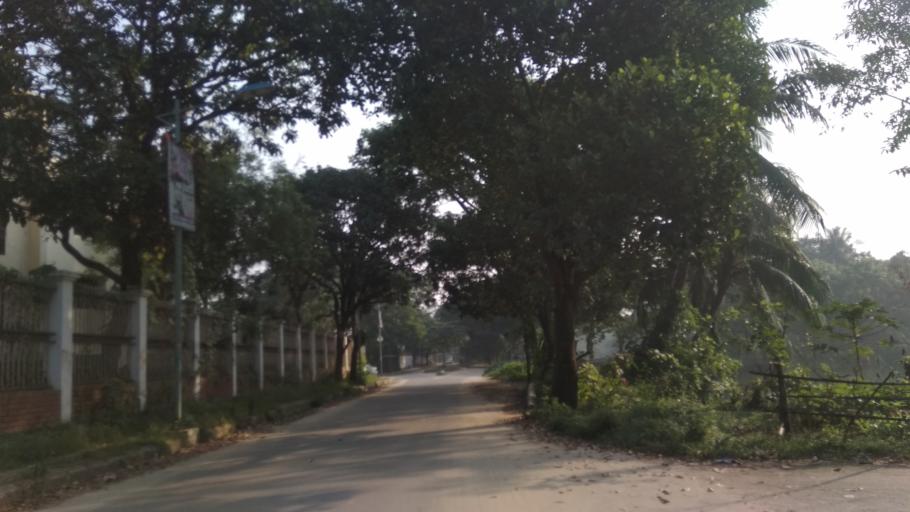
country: BD
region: Dhaka
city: Tungi
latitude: 23.8456
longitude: 90.4166
